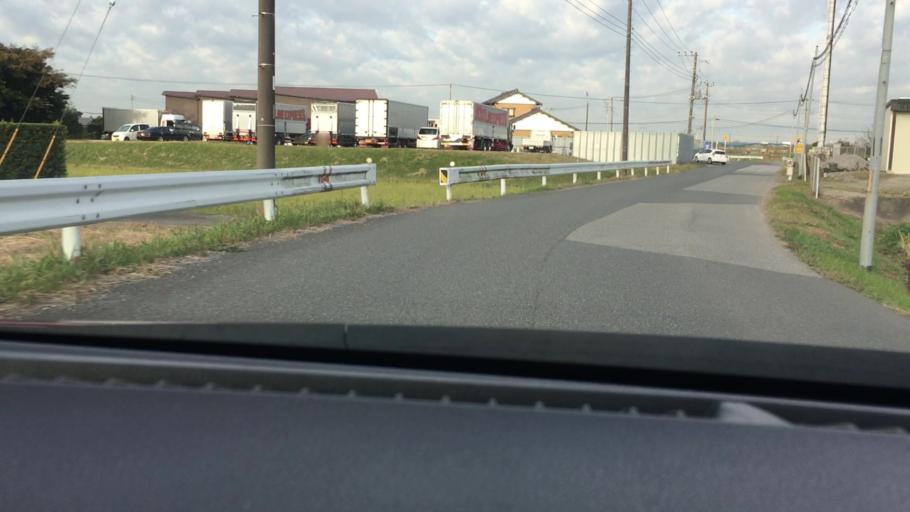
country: JP
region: Chiba
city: Kisarazu
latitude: 35.4073
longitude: 139.9584
